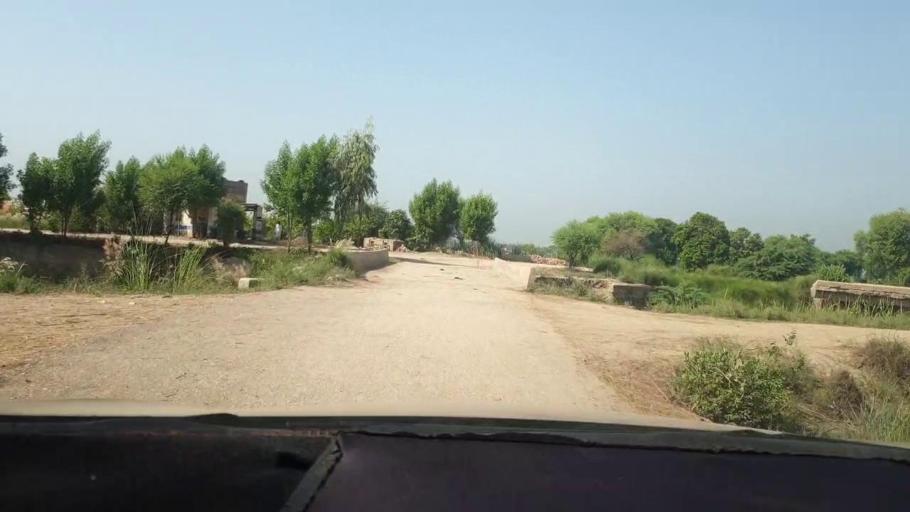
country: PK
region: Sindh
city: Miro Khan
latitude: 27.7029
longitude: 68.0883
